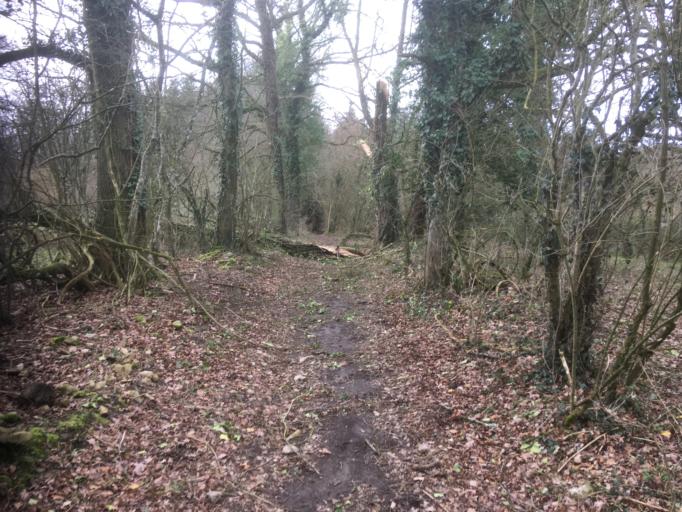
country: BE
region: Wallonia
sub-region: Province du Luxembourg
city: Erezee
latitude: 50.3064
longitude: 5.5004
